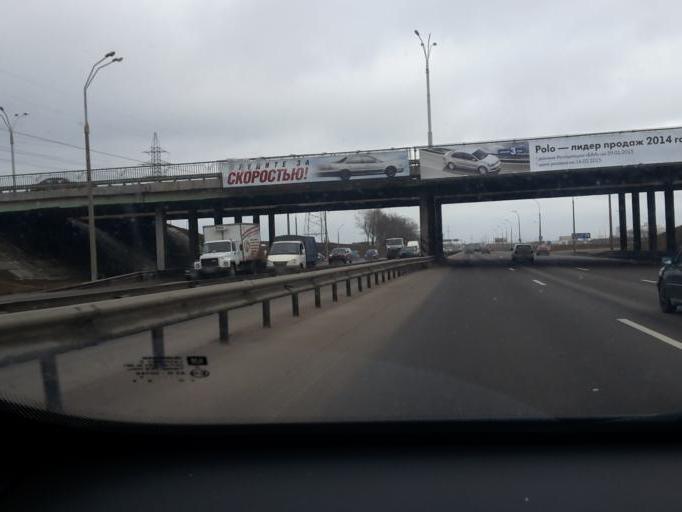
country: BY
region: Minsk
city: Zhdanovichy
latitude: 53.9104
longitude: 27.4095
